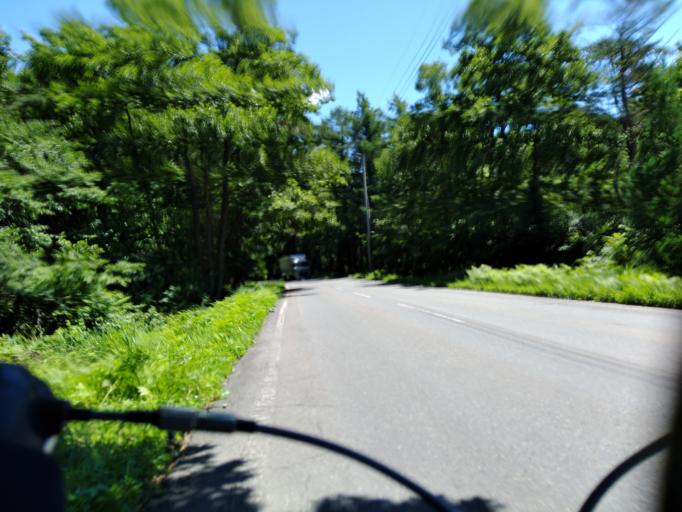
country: JP
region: Iwate
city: Shizukuishi
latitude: 39.7542
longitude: 140.9993
